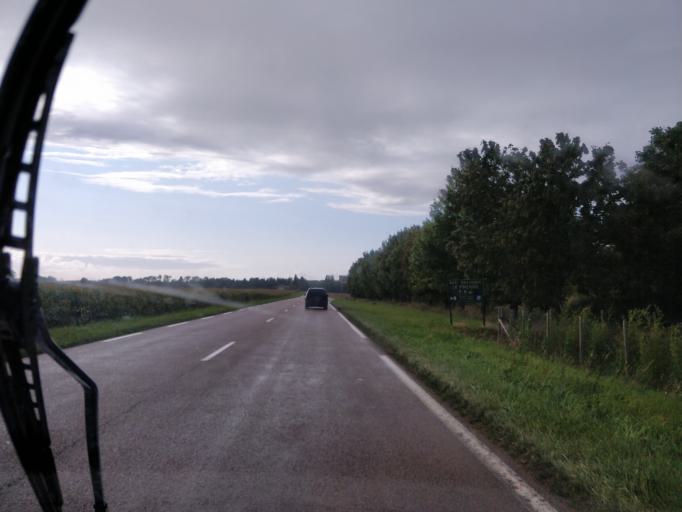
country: FR
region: Champagne-Ardenne
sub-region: Departement de l'Aube
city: Lusigny-sur-Barse
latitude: 48.2450
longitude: 4.2783
